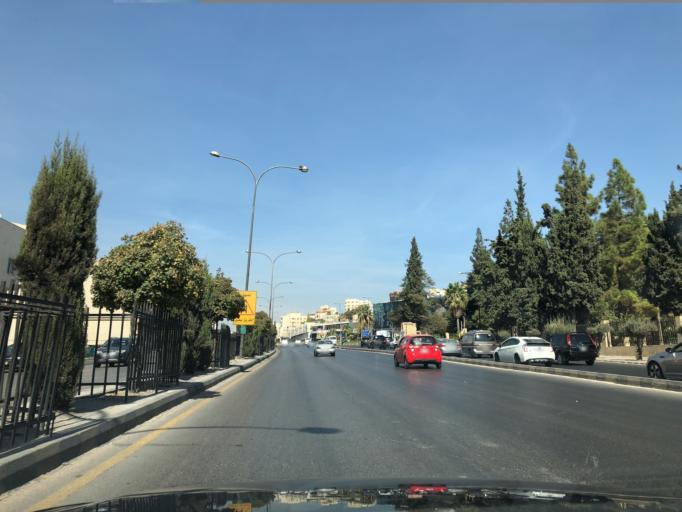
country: JO
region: Amman
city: Al Jubayhah
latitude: 32.0166
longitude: 35.8670
